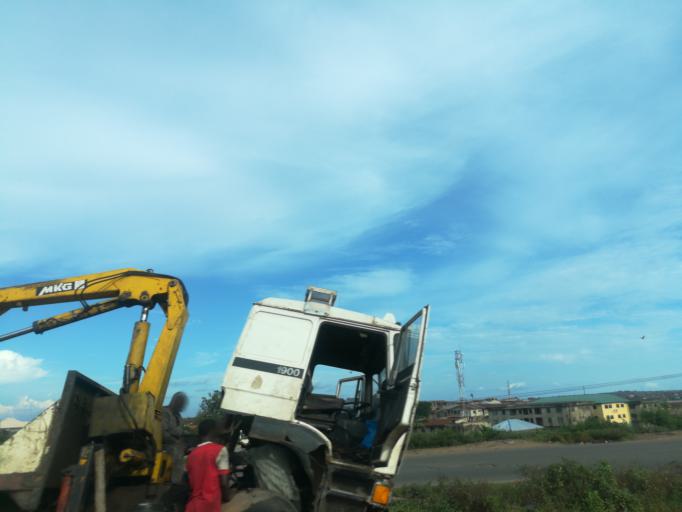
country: NG
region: Oyo
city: Ibadan
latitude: 7.3716
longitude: 3.9292
